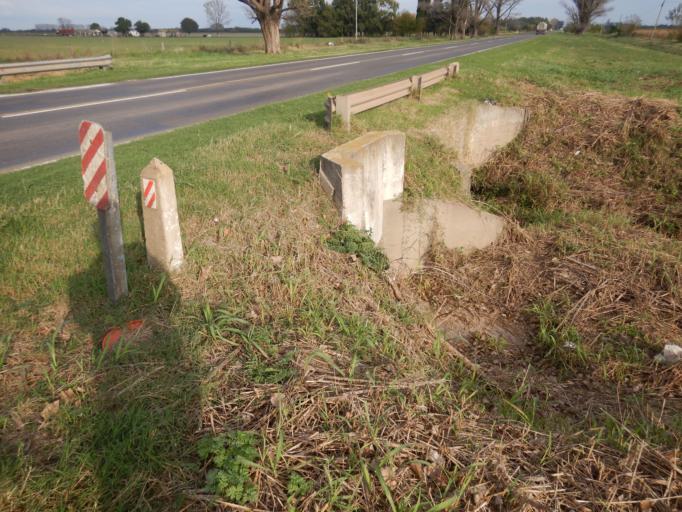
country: AR
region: Santa Fe
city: Roldan
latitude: -32.8962
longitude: -60.9605
